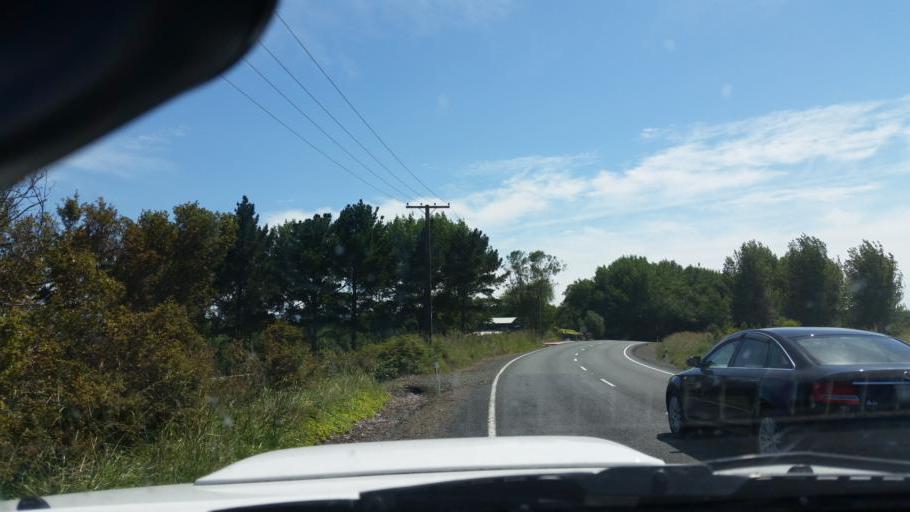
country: NZ
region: Auckland
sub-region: Auckland
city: Wellsford
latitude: -36.2195
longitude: 174.3817
